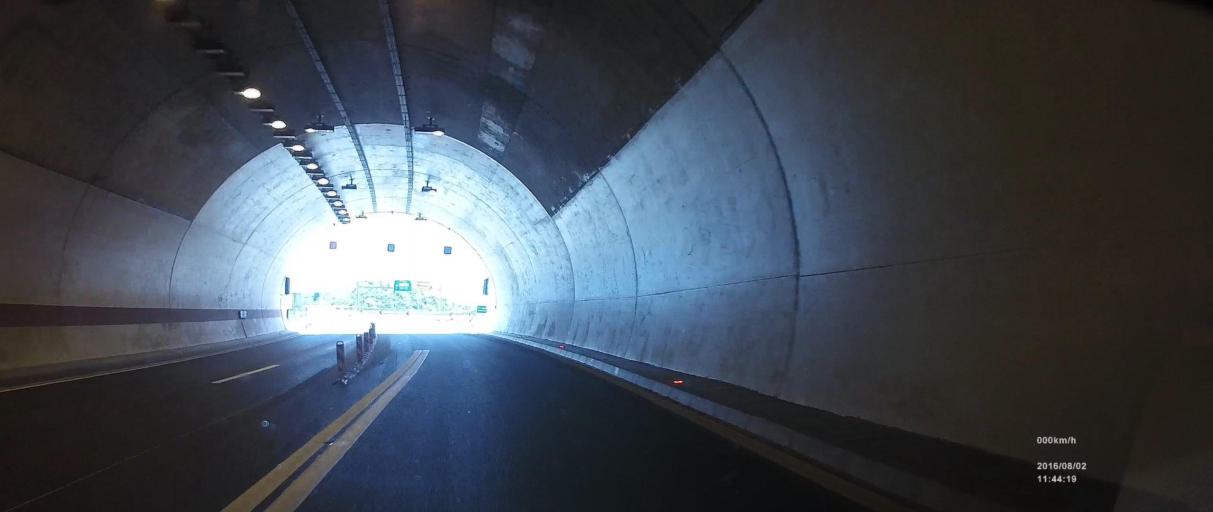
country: HR
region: Dubrovacko-Neretvanska
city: Komin
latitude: 43.0525
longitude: 17.4595
